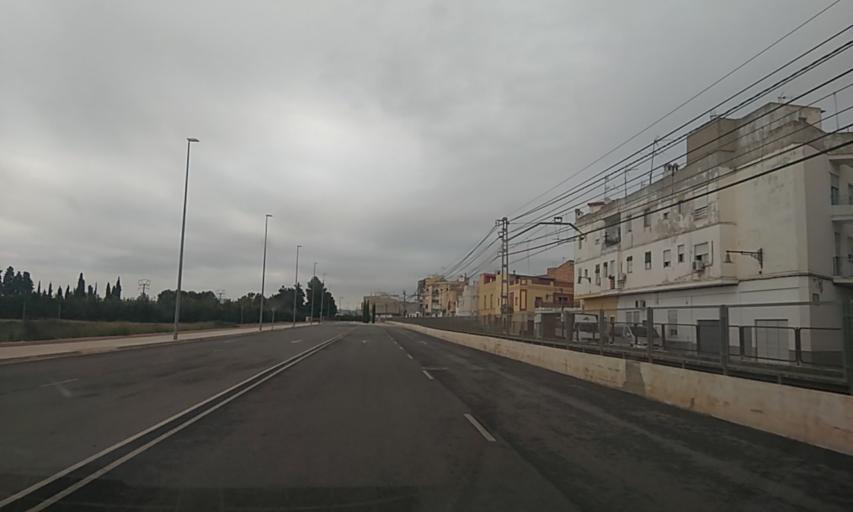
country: ES
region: Valencia
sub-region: Provincia de Valencia
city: L'Alcudia
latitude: 39.1972
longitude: -0.5099
